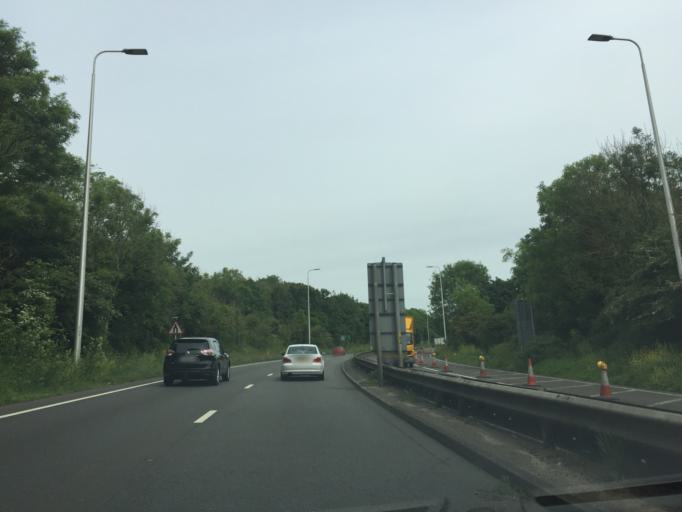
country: GB
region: England
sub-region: Kent
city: Dover
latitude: 51.1304
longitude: 1.3285
